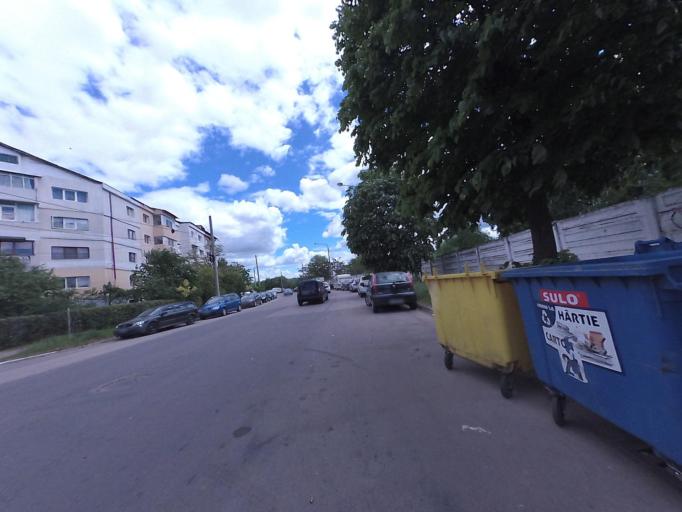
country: RO
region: Vaslui
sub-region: Municipiul Barlad
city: Barlad
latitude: 46.2135
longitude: 27.6638
